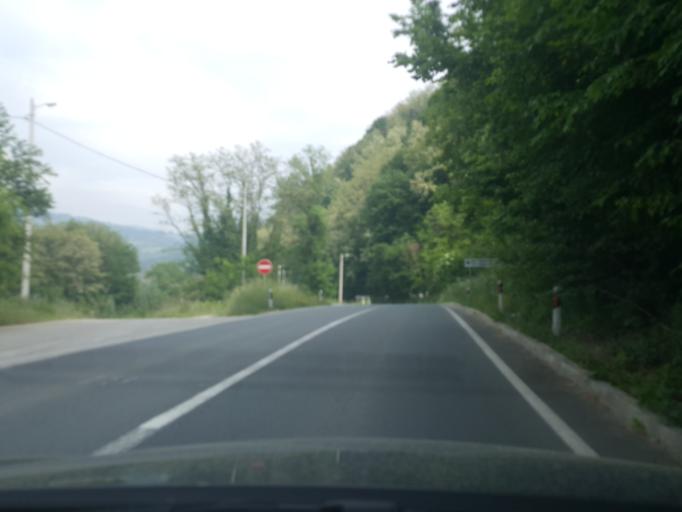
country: RS
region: Central Serbia
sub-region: Zlatiborski Okrug
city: Bajina Basta
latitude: 44.0397
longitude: 19.6207
